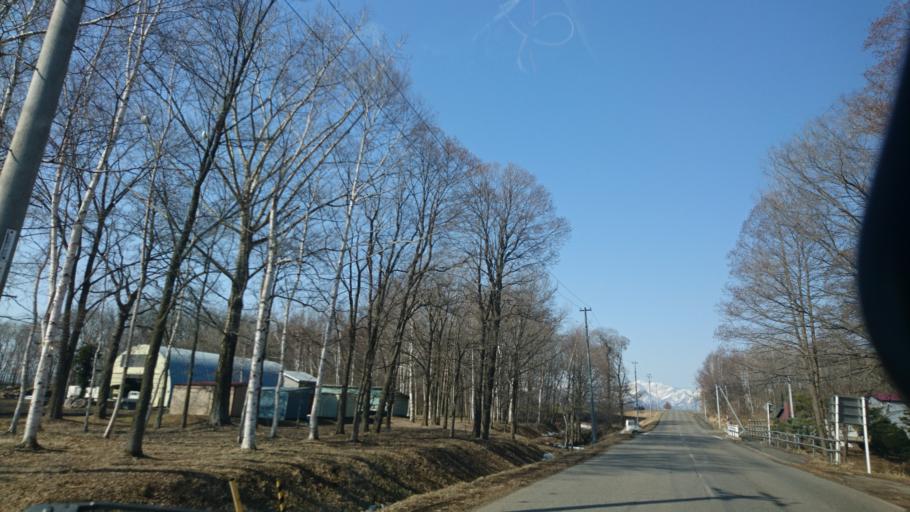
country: JP
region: Hokkaido
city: Obihiro
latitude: 42.9048
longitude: 143.1051
